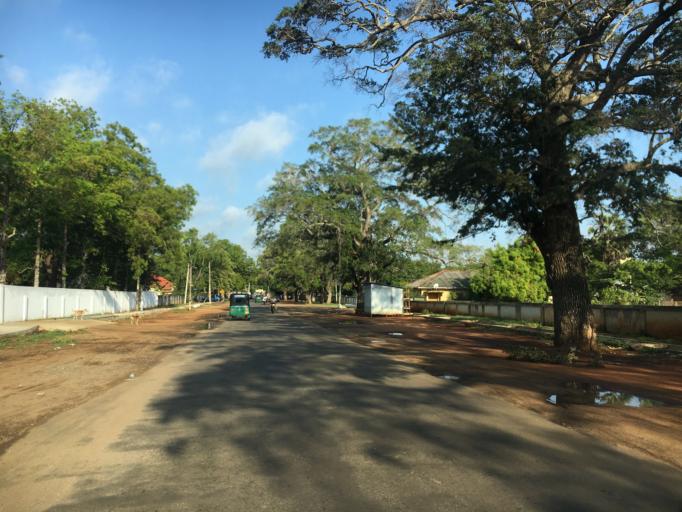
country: LK
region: Northern Province
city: Vavuniya
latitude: 8.7615
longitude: 80.4959
